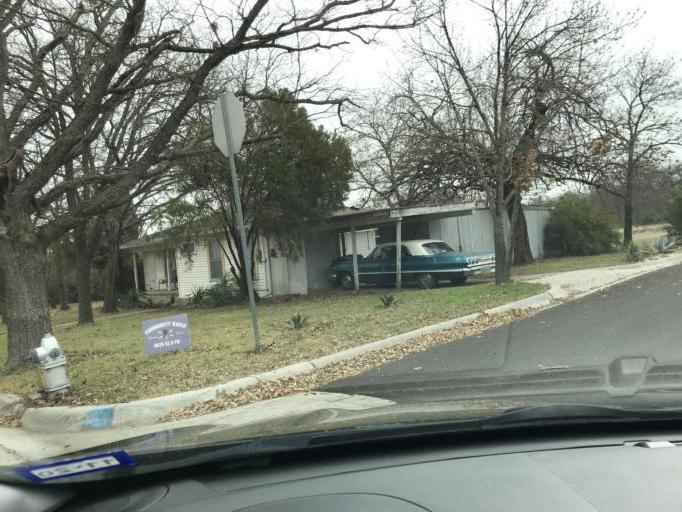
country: US
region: Texas
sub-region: Denton County
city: Denton
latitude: 33.2217
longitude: -97.1533
